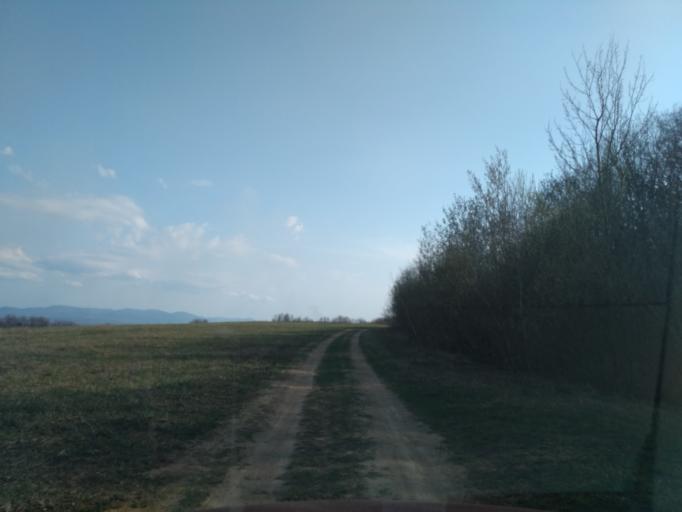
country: SK
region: Kosicky
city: Kosice
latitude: 48.6802
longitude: 21.1814
